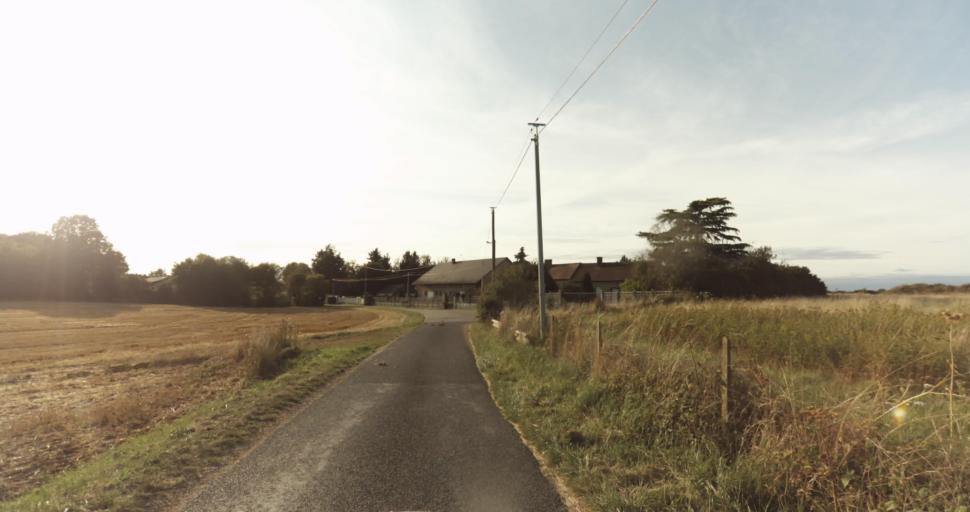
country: FR
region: Haute-Normandie
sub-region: Departement de l'Eure
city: Marcilly-sur-Eure
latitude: 48.8825
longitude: 1.2714
